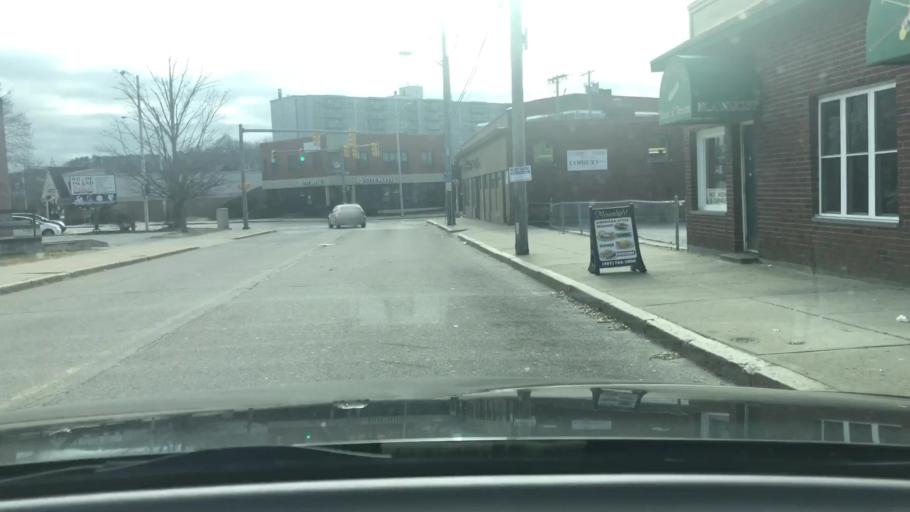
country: US
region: Rhode Island
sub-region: Providence County
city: Woonsocket
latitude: 42.0094
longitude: -71.5038
